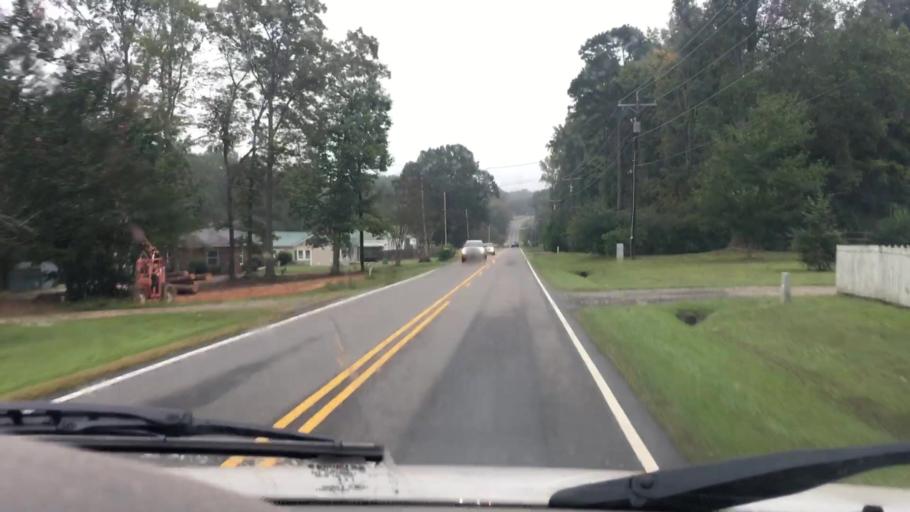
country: US
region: North Carolina
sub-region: Iredell County
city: Mooresville
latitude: 35.6308
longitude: -80.7786
